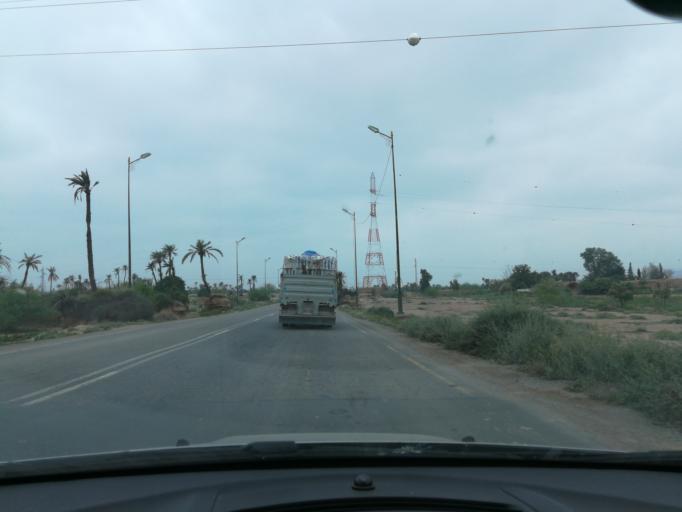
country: MA
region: Marrakech-Tensift-Al Haouz
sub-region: Marrakech
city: Marrakesh
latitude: 31.6883
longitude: -7.9997
